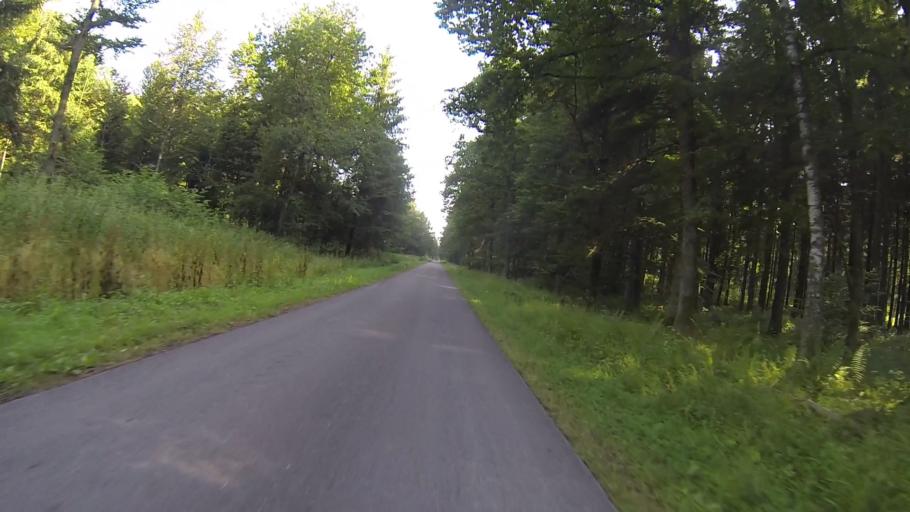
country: DE
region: Baden-Wuerttemberg
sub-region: Regierungsbezirk Stuttgart
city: Konigsbronn
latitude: 48.7181
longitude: 10.1120
